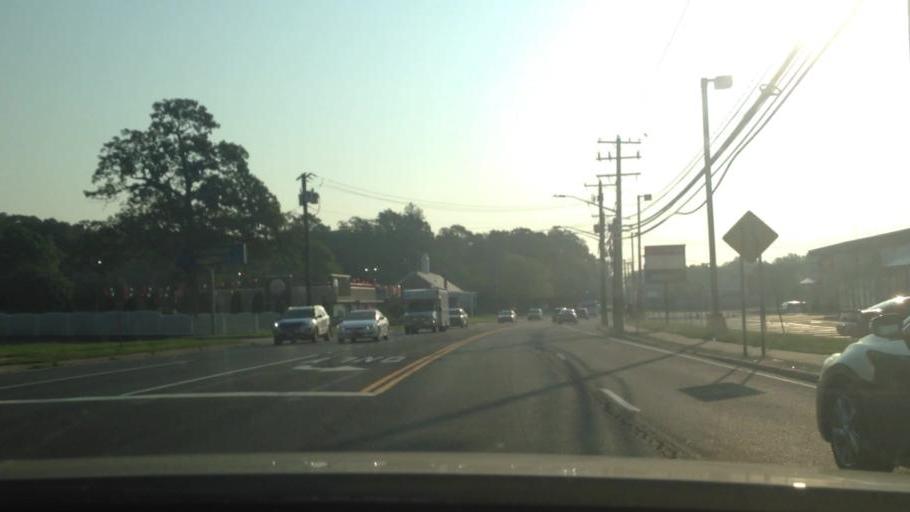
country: US
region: New York
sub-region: Suffolk County
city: Coram
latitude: 40.8703
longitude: -72.9984
